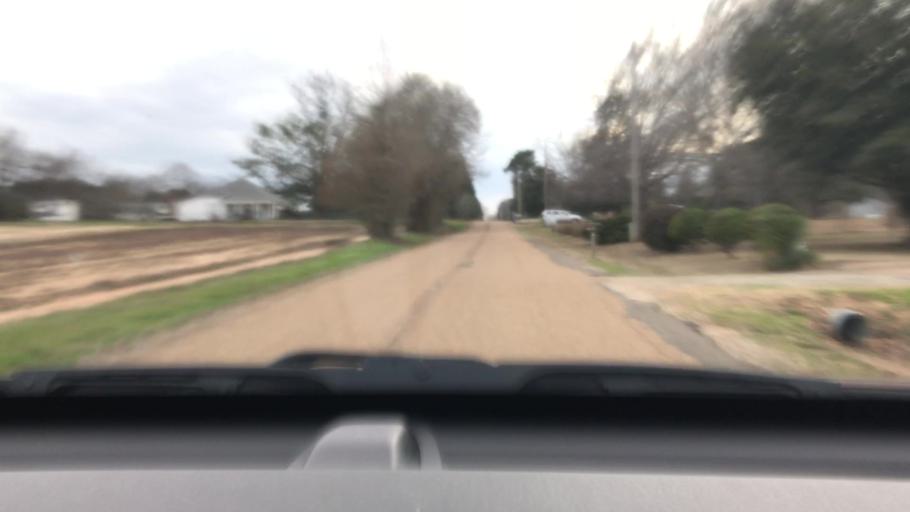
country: US
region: Arkansas
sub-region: Hempstead County
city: Hope
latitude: 33.6386
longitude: -93.5632
